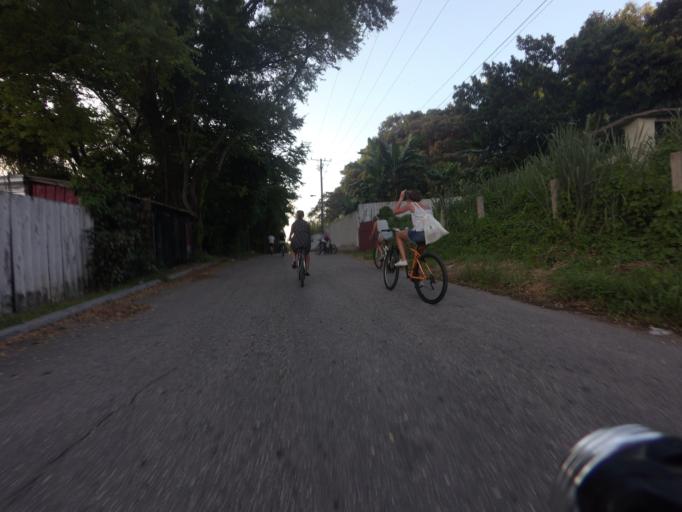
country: CU
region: La Habana
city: Cerro
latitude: 23.1125
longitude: -82.4052
